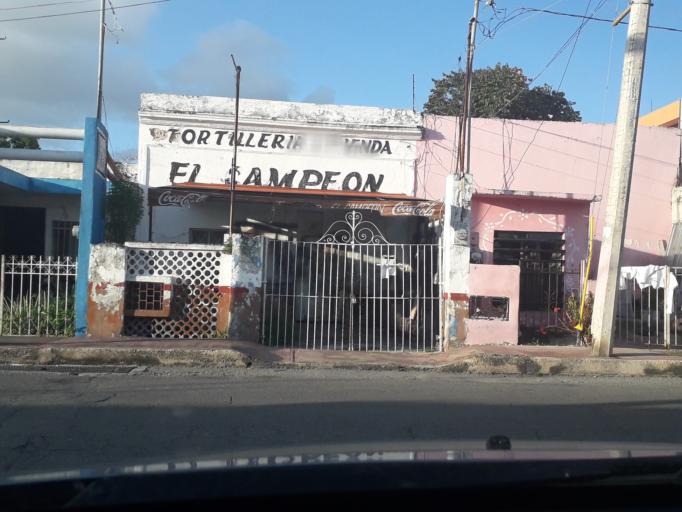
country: MX
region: Yucatan
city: Merida
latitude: 20.9722
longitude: -89.6454
